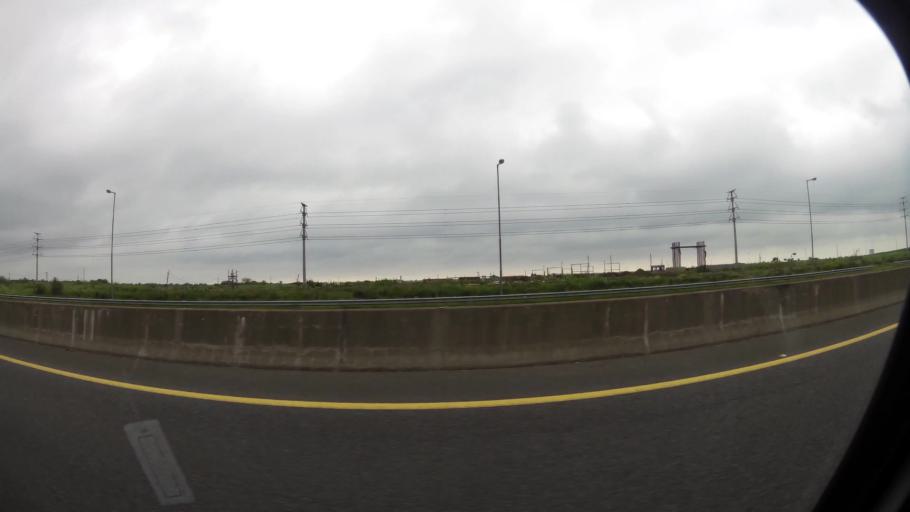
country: AR
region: Buenos Aires
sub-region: Partido de Quilmes
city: Quilmes
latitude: -34.7865
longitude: -58.1464
